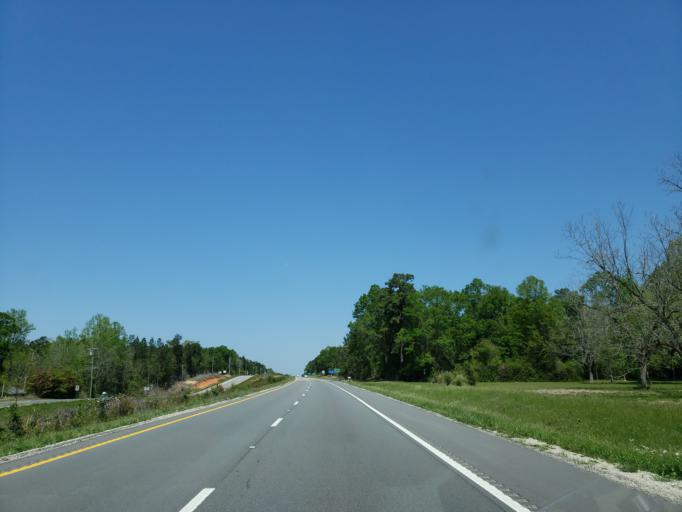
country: US
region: Mississippi
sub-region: Stone County
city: Wiggins
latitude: 30.9088
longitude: -89.1703
